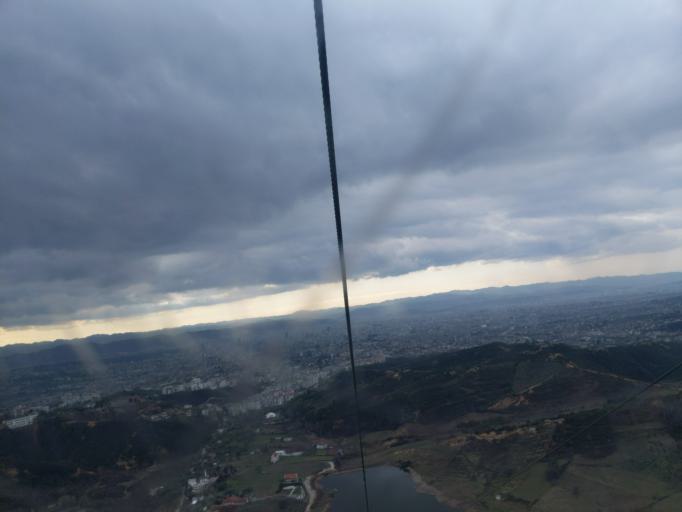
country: AL
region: Tirane
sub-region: Rrethi i Tiranes
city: Dajt
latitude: 41.3595
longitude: 19.8832
